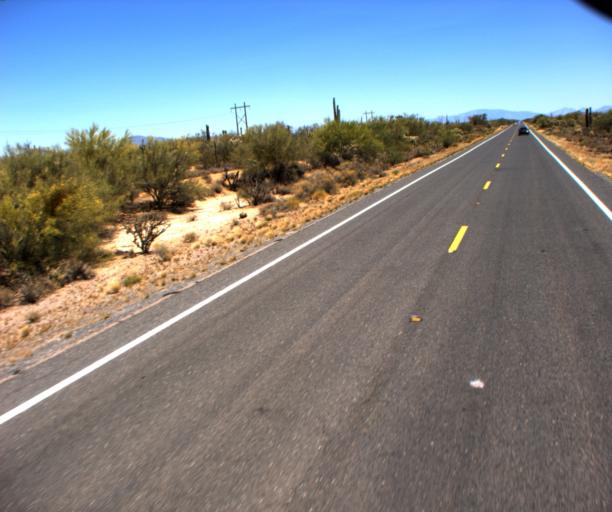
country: US
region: Arizona
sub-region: Pinal County
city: Florence
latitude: 32.8419
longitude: -111.2226
